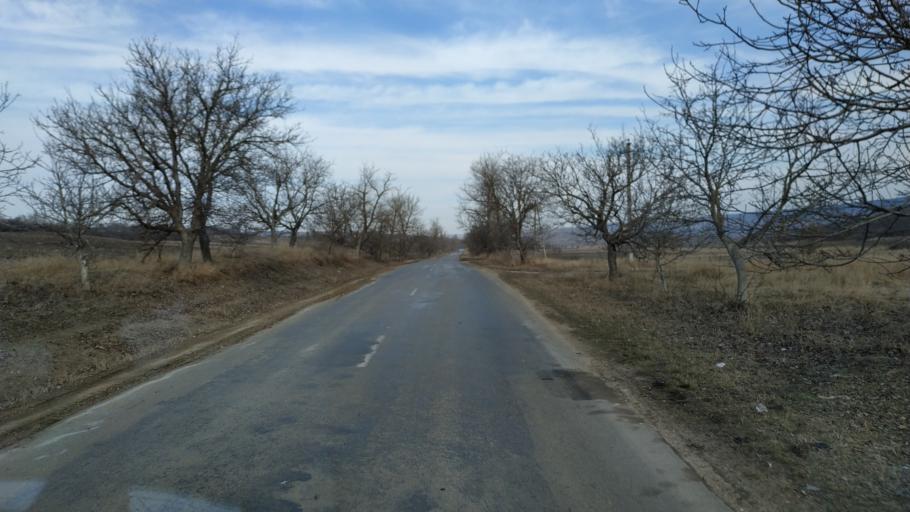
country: MD
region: Nisporeni
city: Nisporeni
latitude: 47.1127
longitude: 28.1237
